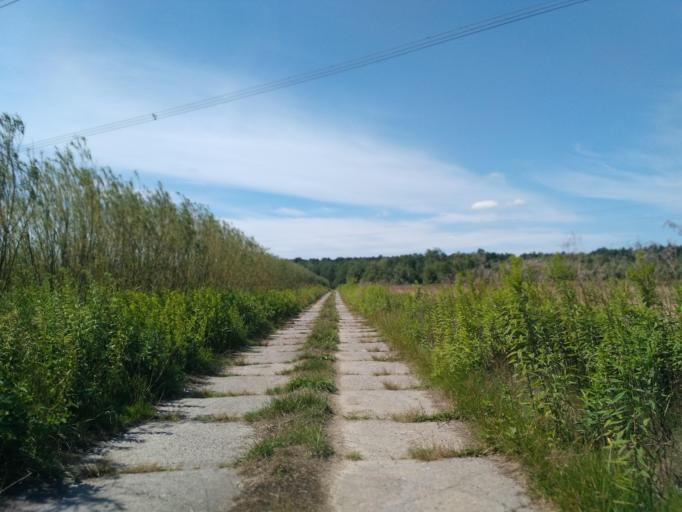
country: PL
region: Subcarpathian Voivodeship
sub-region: Powiat krosnienski
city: Kroscienko Wyzne
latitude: 49.6494
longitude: 21.8558
